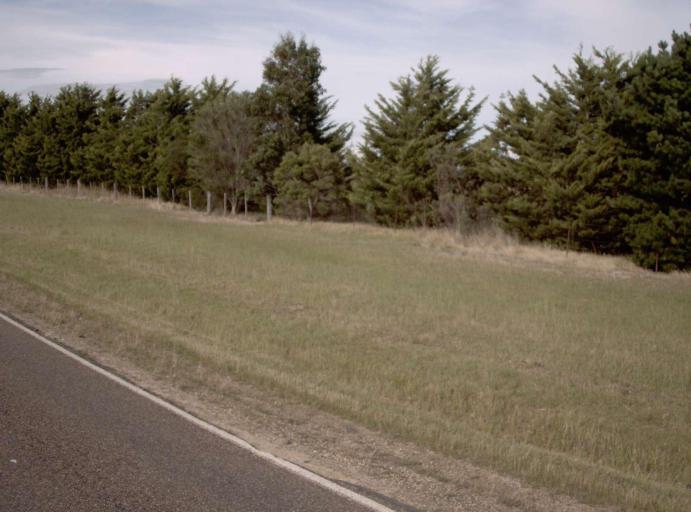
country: AU
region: Victoria
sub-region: Wellington
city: Heyfield
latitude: -38.0413
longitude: 146.6657
